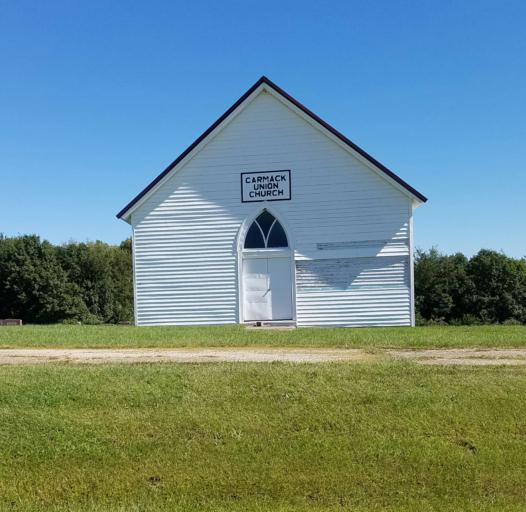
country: US
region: Missouri
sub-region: Gentry County
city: Albany
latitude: 40.2440
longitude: -94.4268
